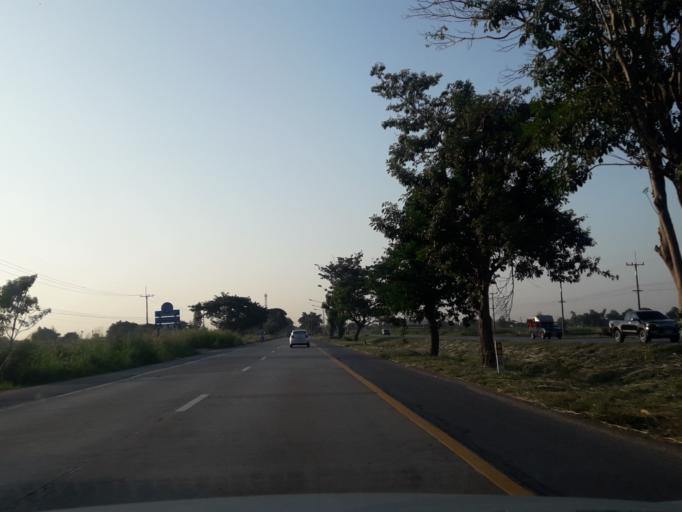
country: TH
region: Phra Nakhon Si Ayutthaya
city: Bang Pa-in
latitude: 14.2691
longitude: 100.5316
